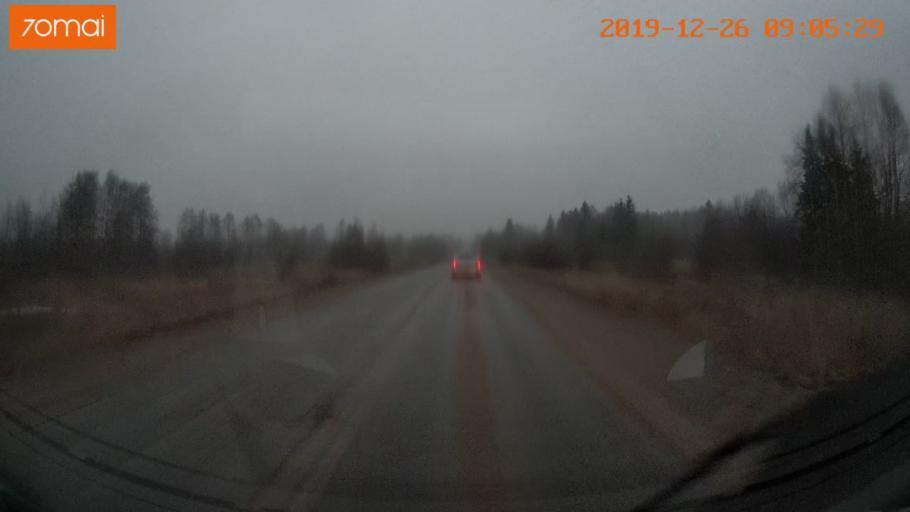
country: RU
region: Vologda
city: Gryazovets
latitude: 58.8260
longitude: 40.2577
